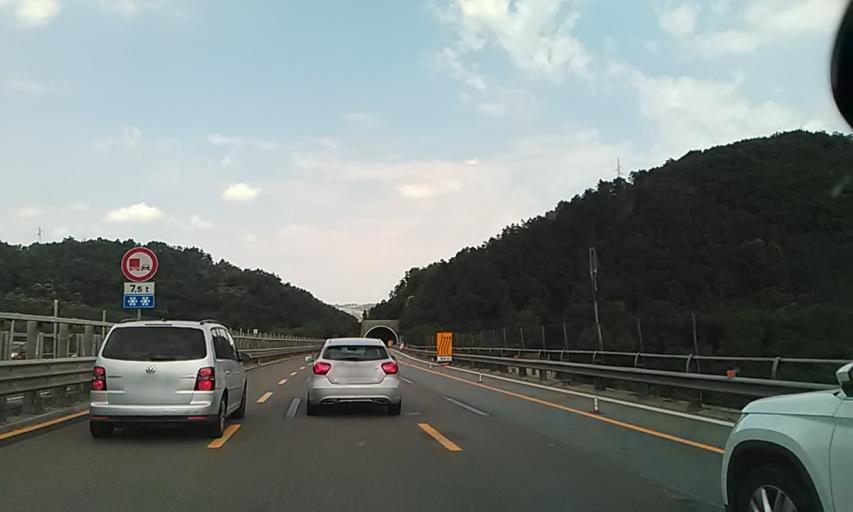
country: IT
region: Piedmont
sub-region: Provincia di Alessandria
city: Belforte Monferrato
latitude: 44.6150
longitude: 8.6566
